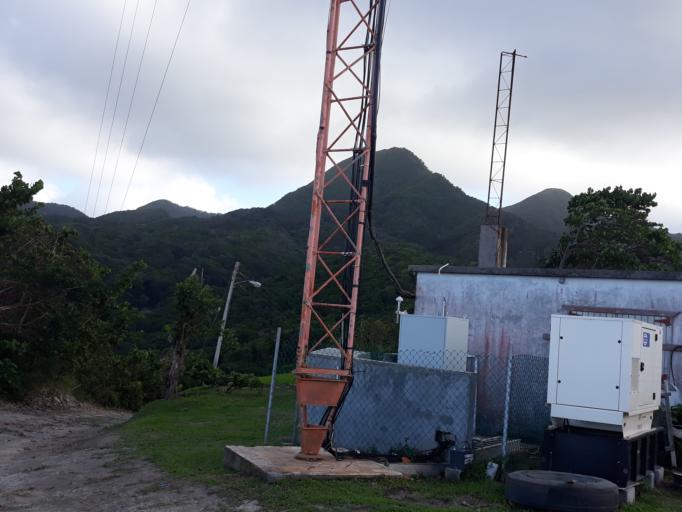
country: MS
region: Saint Peter
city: Brades
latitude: 16.7781
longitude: -62.1980
